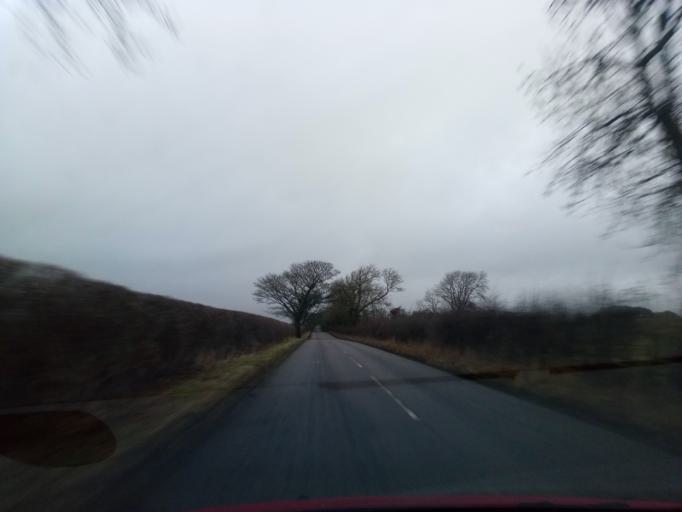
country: GB
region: England
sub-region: Northumberland
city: Rothley
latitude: 55.1881
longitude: -1.9701
